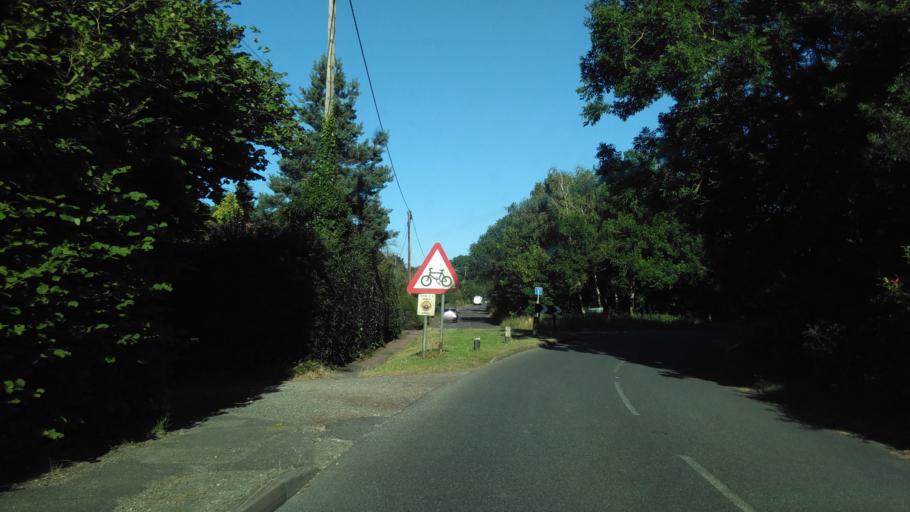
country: GB
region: England
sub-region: Kent
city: Dunkirk
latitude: 51.2906
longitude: 0.9895
